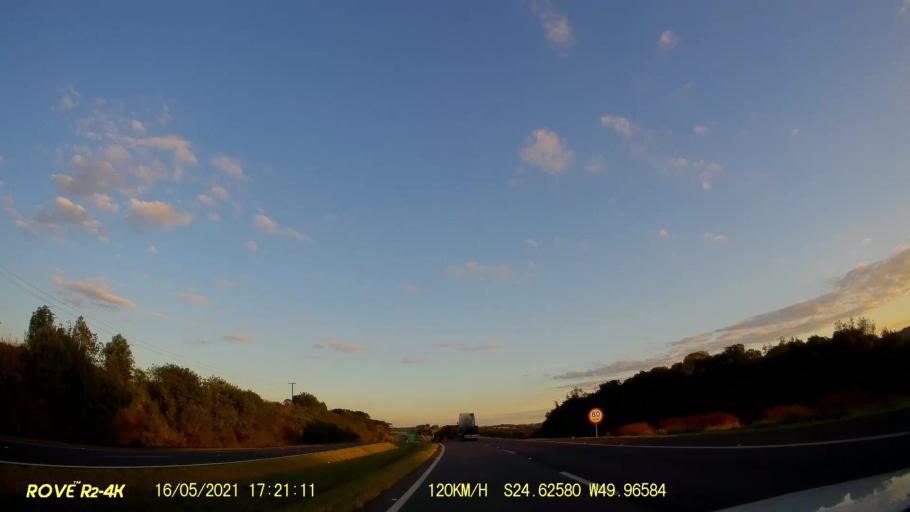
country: BR
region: Parana
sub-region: Pirai Do Sul
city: Pirai do Sul
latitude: -24.6263
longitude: -49.9659
